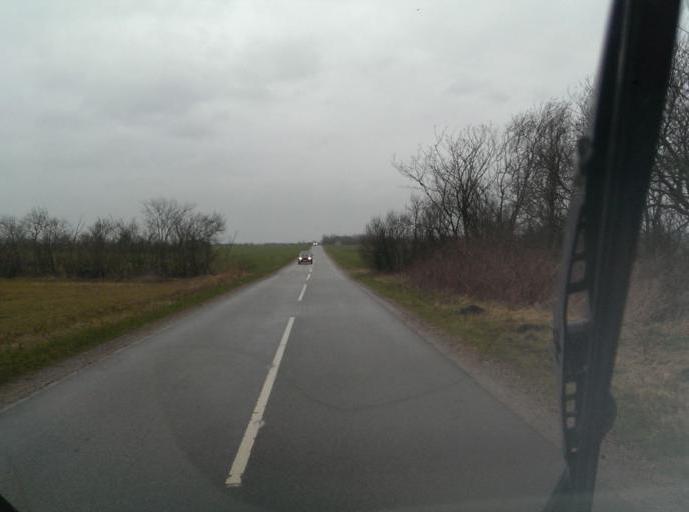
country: DK
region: Central Jutland
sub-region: Ringkobing-Skjern Kommune
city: Skjern
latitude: 56.0538
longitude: 8.4590
